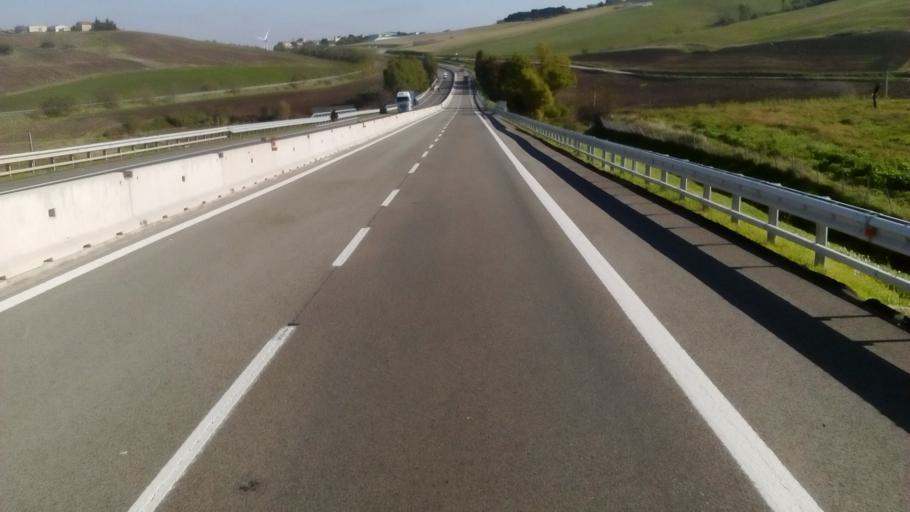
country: IT
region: Apulia
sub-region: Provincia di Foggia
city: Candela
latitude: 41.1488
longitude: 15.5053
